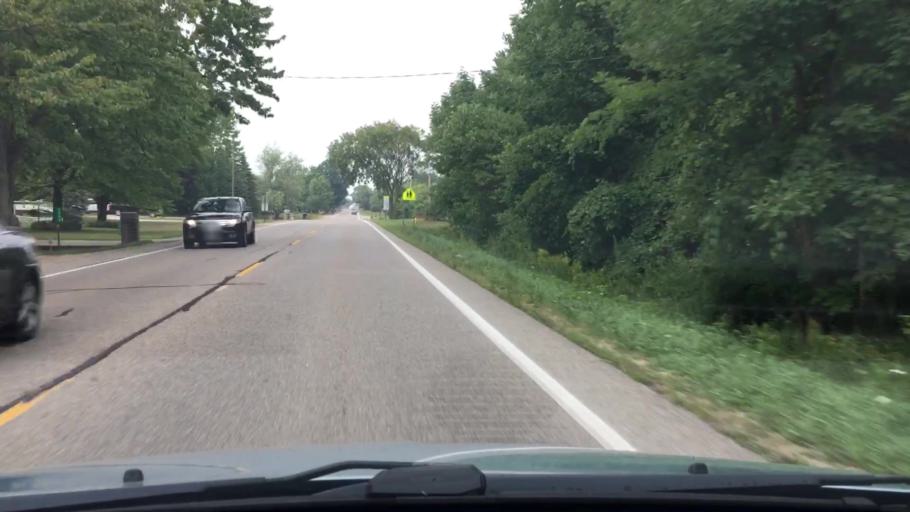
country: US
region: Michigan
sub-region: Ottawa County
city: Hudsonville
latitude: 42.9135
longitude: -85.9023
